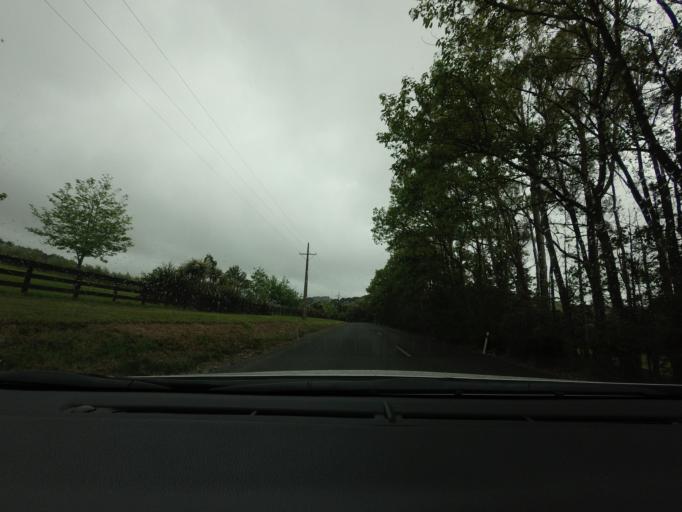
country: NZ
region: Auckland
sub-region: Auckland
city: Wellsford
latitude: -36.2845
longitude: 174.6119
